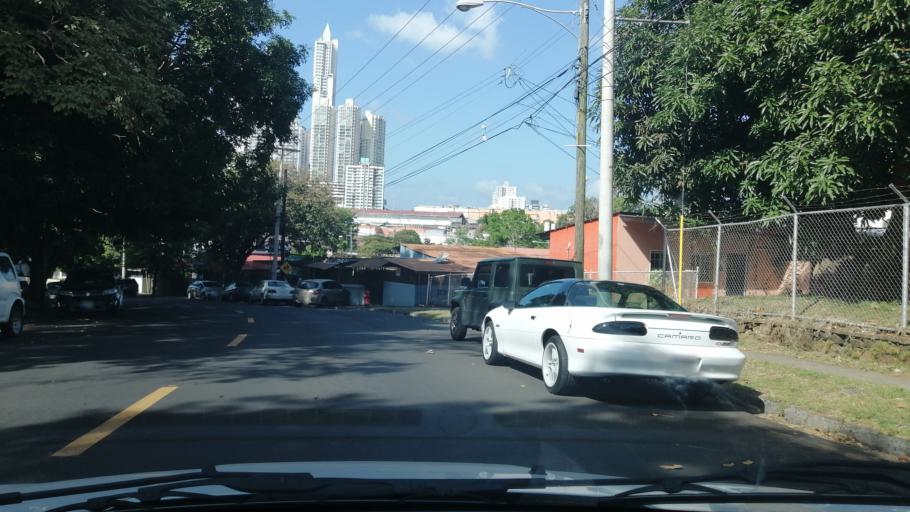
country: PA
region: Panama
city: Panama
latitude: 9.0065
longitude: -79.5283
